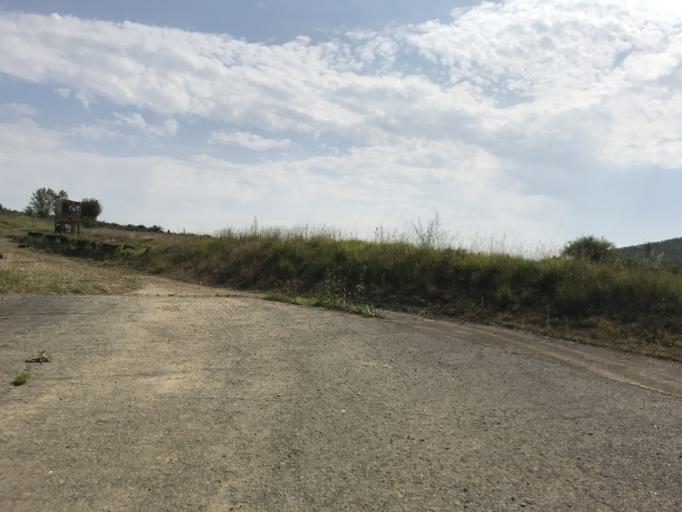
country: ES
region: Basque Country
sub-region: Provincia de Alava
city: Gasteiz / Vitoria
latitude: 42.8183
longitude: -2.6433
